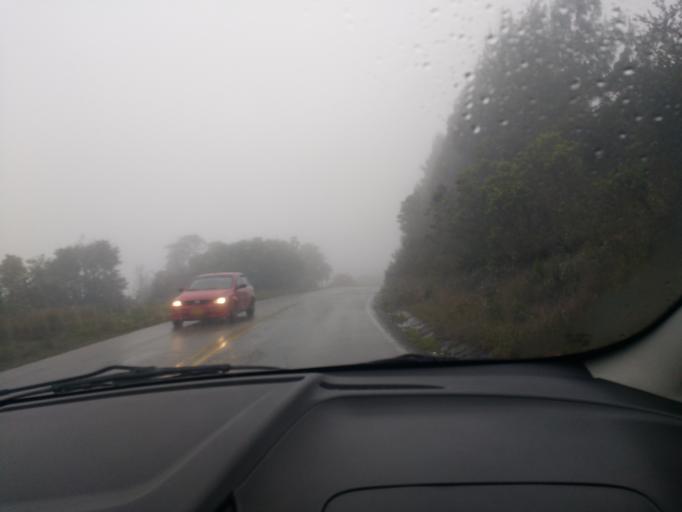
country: CO
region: Bogota D.C.
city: Bogota
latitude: 4.5848
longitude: -74.0231
